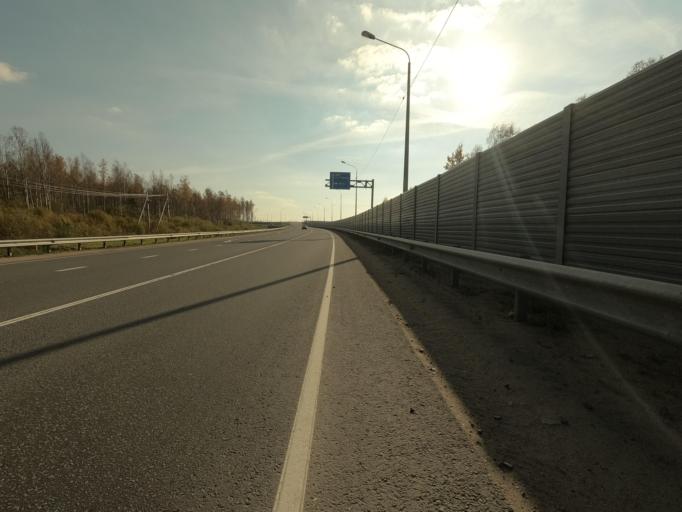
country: RU
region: Leningrad
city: Mga
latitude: 59.7618
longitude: 31.0941
